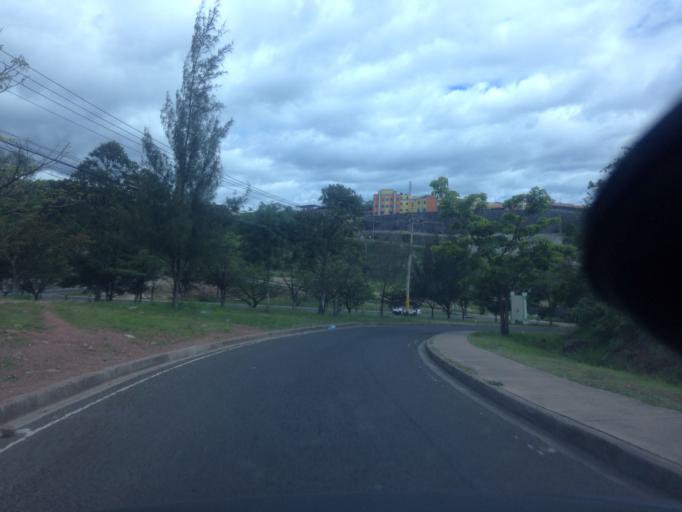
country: HN
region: Francisco Morazan
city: Tegucigalpa
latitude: 14.0821
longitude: -87.1624
